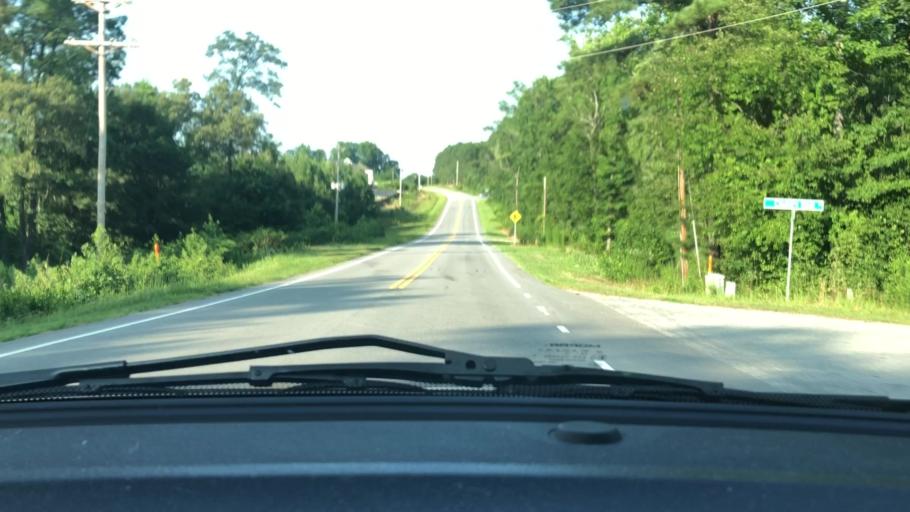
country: US
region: North Carolina
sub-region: Lee County
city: Broadway
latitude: 35.3266
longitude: -79.0625
